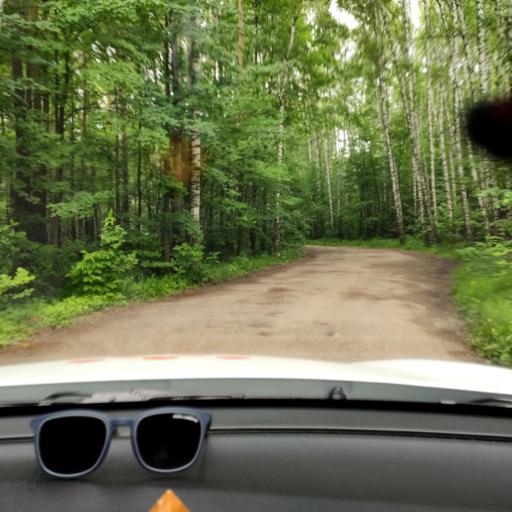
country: RU
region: Tatarstan
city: Vysokaya Gora
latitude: 55.9293
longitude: 49.1625
